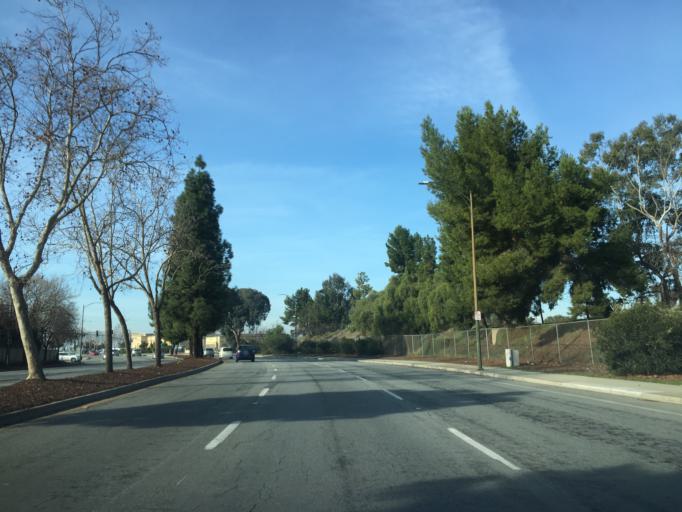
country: US
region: California
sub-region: Santa Clara County
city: Alum Rock
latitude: 37.3334
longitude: -121.8085
